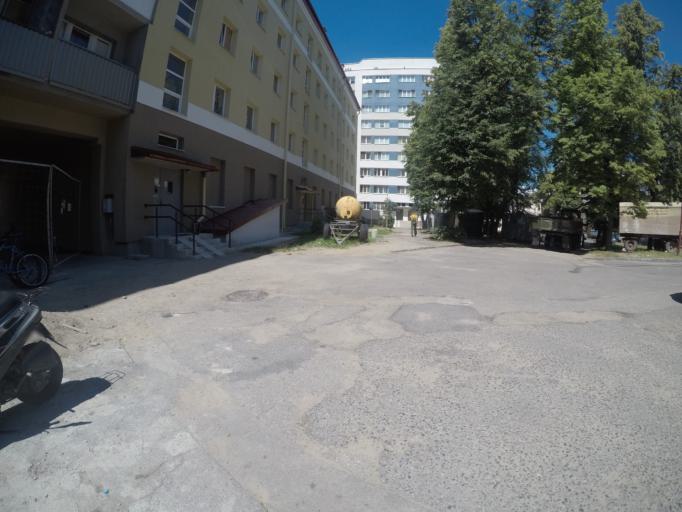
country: BY
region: Grodnenskaya
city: Hrodna
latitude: 53.6983
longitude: 23.8207
